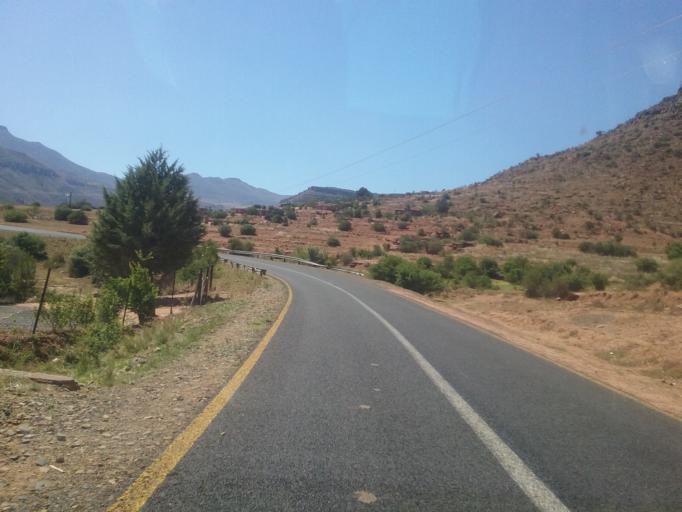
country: LS
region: Quthing
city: Quthing
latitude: -30.3390
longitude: 27.7395
